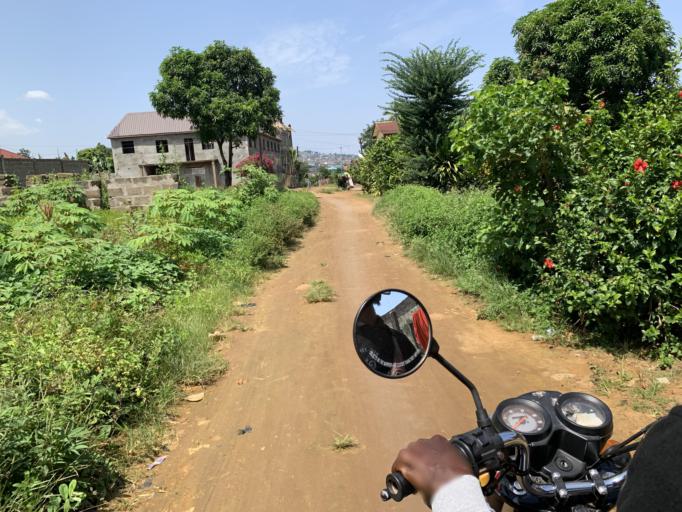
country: SL
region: Western Area
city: Hastings
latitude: 8.3820
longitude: -13.1379
